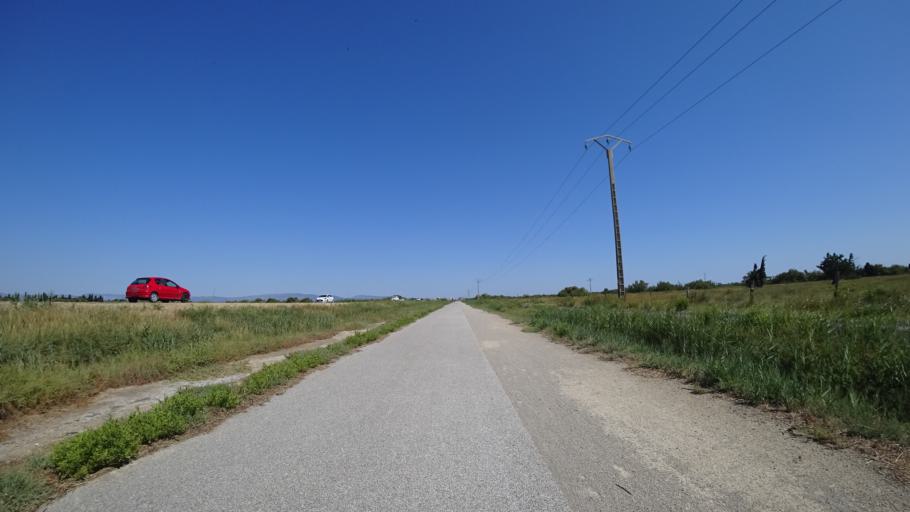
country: FR
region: Languedoc-Roussillon
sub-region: Departement des Pyrenees-Orientales
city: Sainte-Marie-Plage
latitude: 42.7466
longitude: 3.0229
